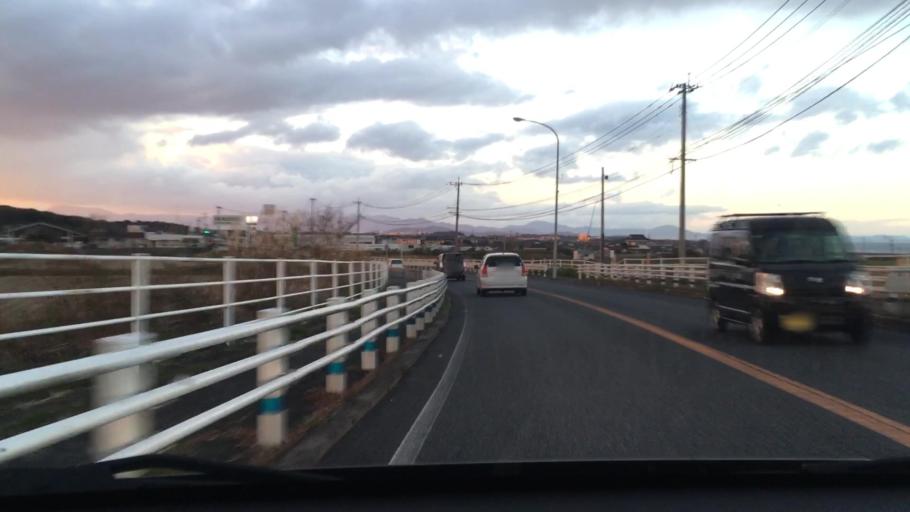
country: JP
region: Fukuoka
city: Shiida
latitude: 33.6282
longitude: 131.0874
